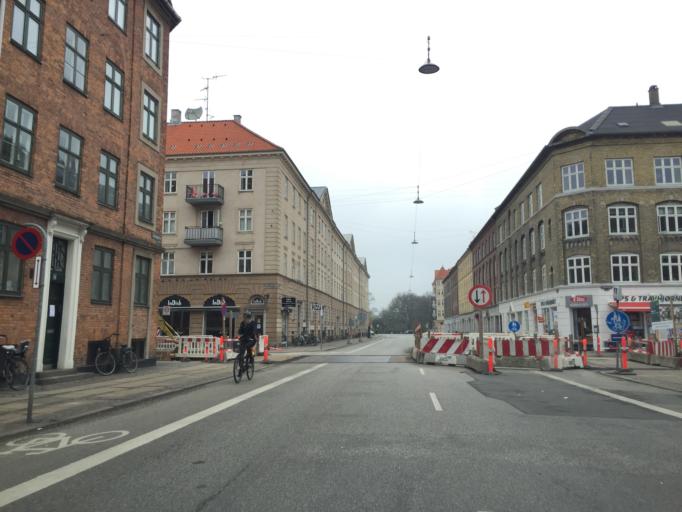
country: DK
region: Capital Region
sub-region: Kobenhavn
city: Copenhagen
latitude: 55.7125
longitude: 12.5691
